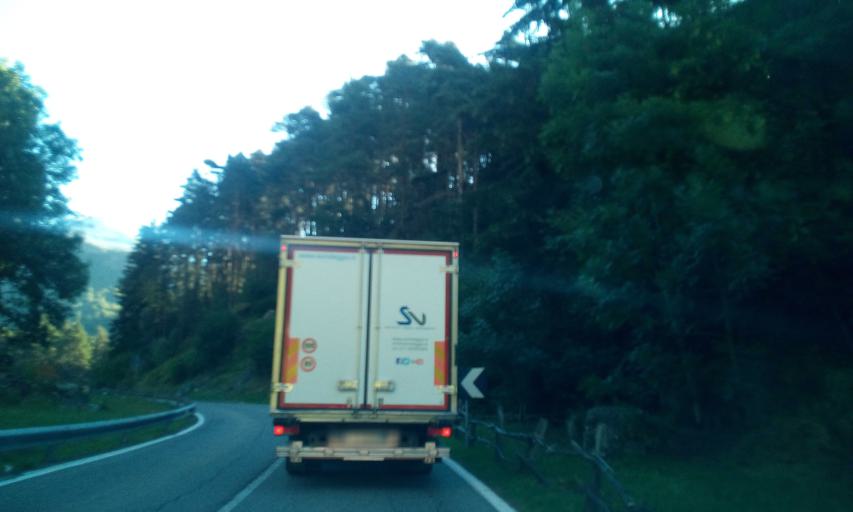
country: IT
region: Aosta Valley
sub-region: Valle d'Aosta
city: Quincod
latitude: 45.7324
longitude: 7.7444
